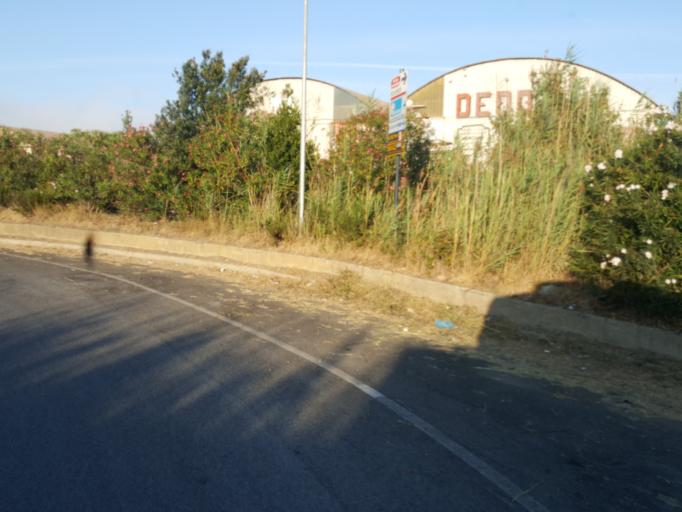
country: IT
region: Latium
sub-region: Citta metropolitana di Roma Capitale
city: Aurelia
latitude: 42.1189
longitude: 11.7703
